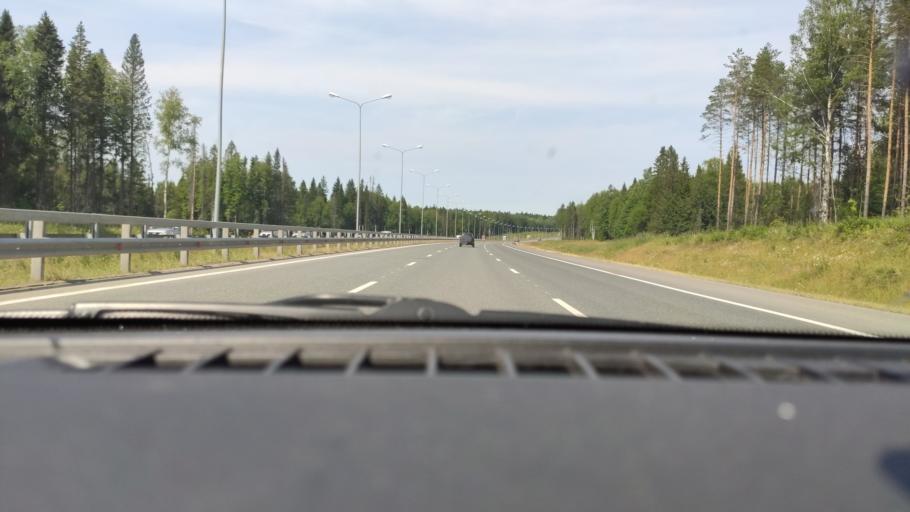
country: RU
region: Perm
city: Zvezdnyy
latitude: 57.7503
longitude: 56.3341
